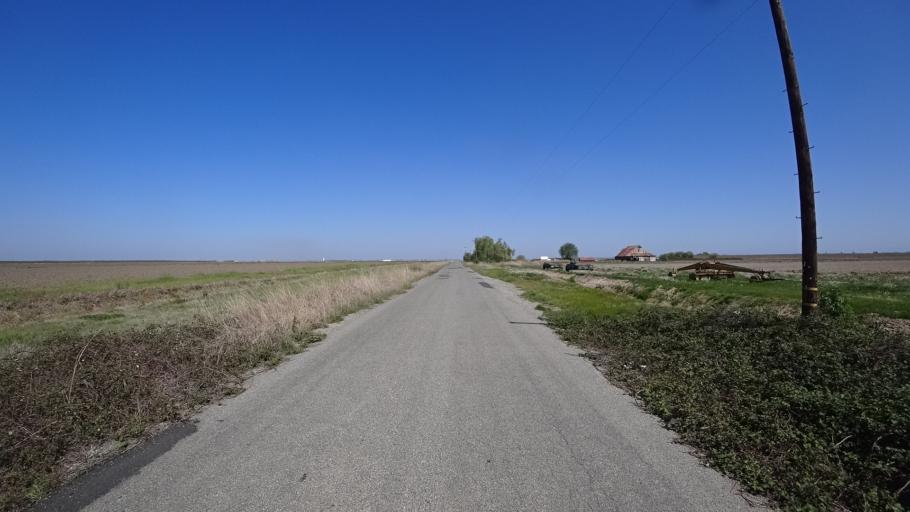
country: US
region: California
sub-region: Glenn County
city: Willows
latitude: 39.5095
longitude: -122.0373
